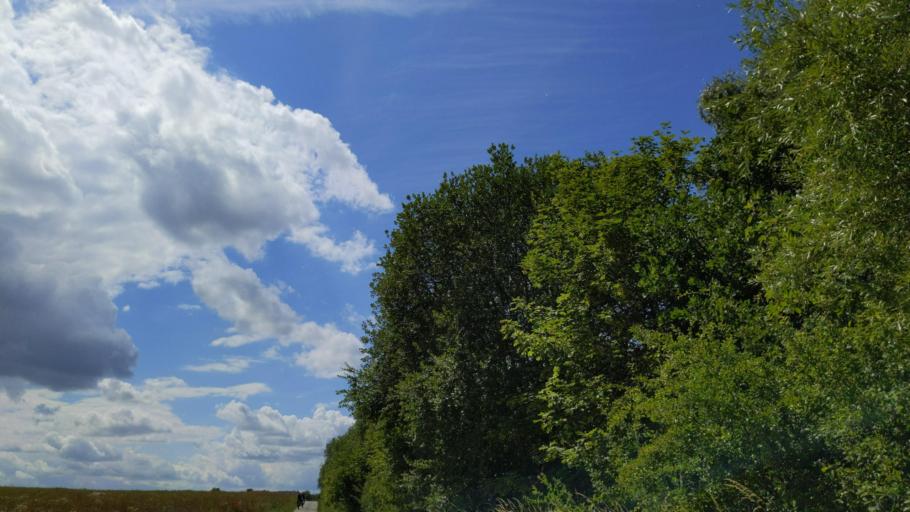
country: DE
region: Mecklenburg-Vorpommern
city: Kalkhorst
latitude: 54.0115
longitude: 11.0854
